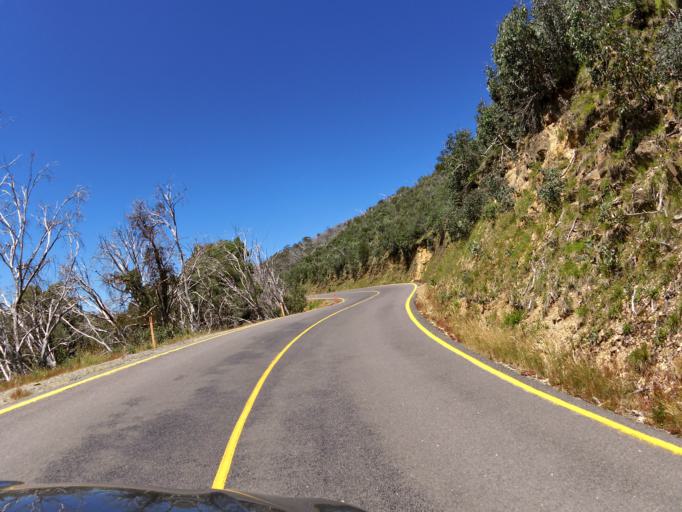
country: AU
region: Victoria
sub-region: Alpine
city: Mount Beauty
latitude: -37.0047
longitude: 147.0758
